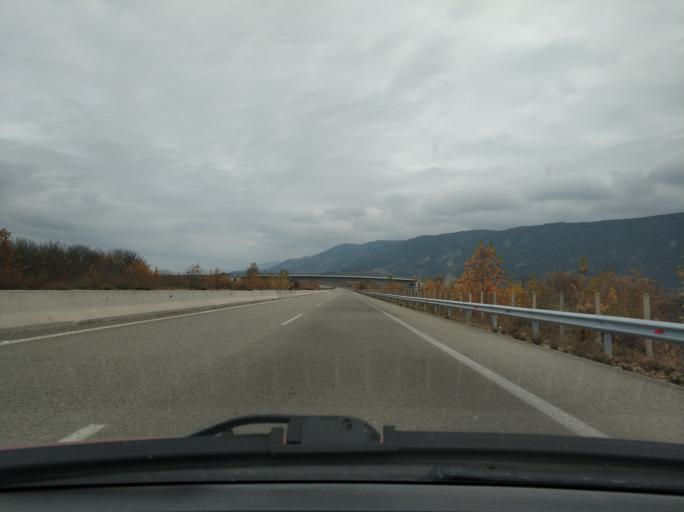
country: GR
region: East Macedonia and Thrace
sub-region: Nomos Kavalas
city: Nikisiani
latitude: 40.8237
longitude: 24.0776
